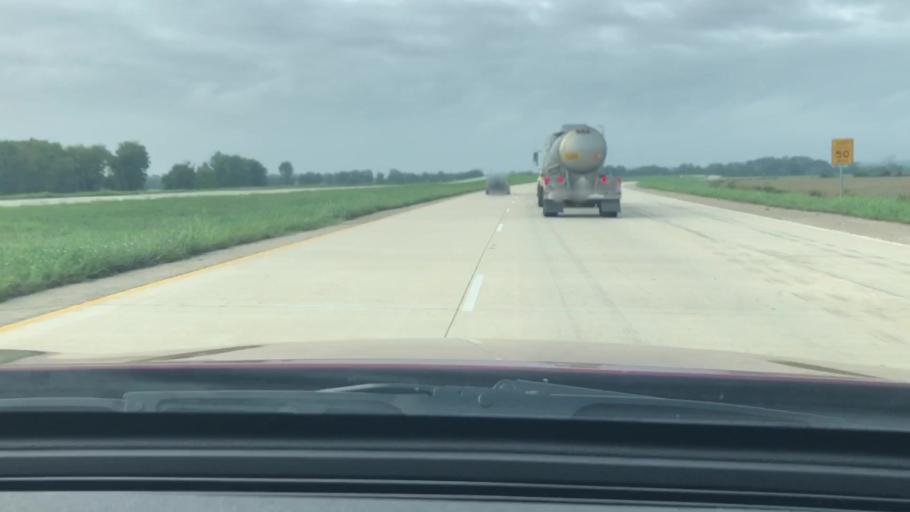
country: US
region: Louisiana
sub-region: Caddo Parish
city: Vivian
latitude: 32.8572
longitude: -93.8622
